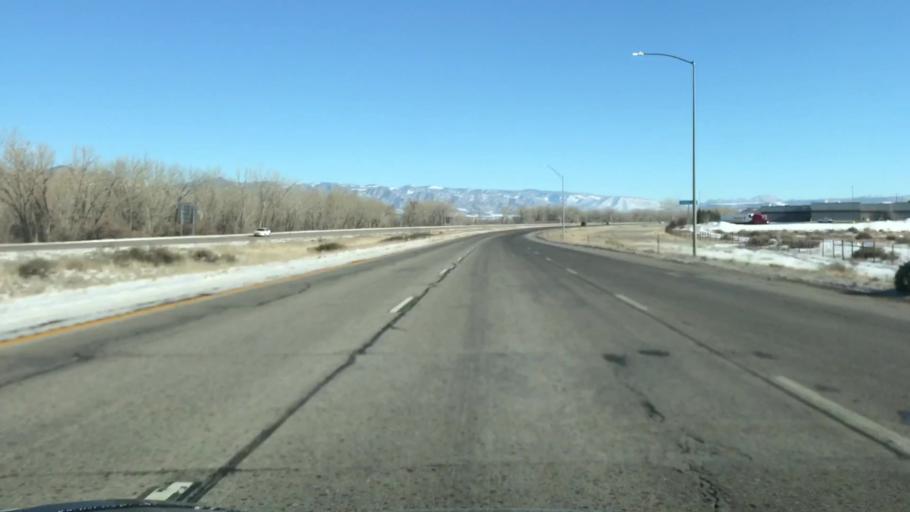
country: US
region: Colorado
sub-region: Garfield County
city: Rifle
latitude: 39.5253
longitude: -107.7728
